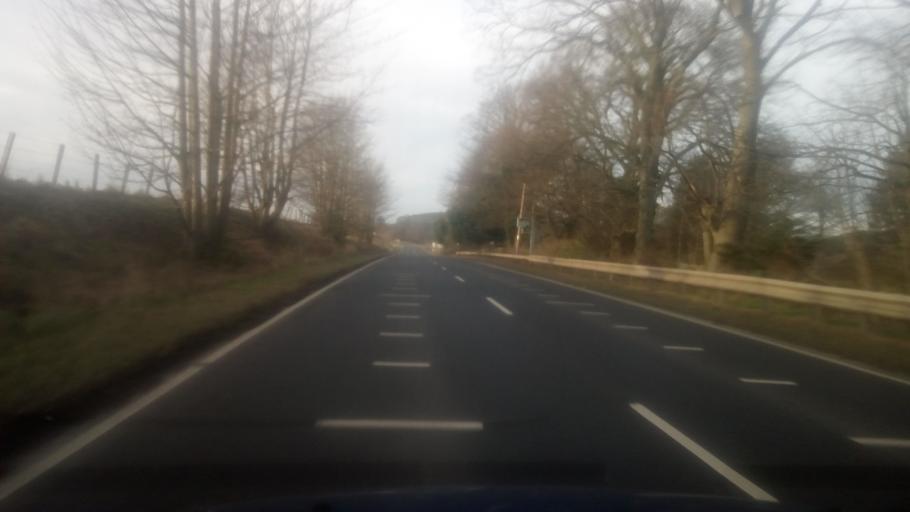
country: GB
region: Scotland
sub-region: The Scottish Borders
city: Jedburgh
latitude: 55.4277
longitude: -2.5310
